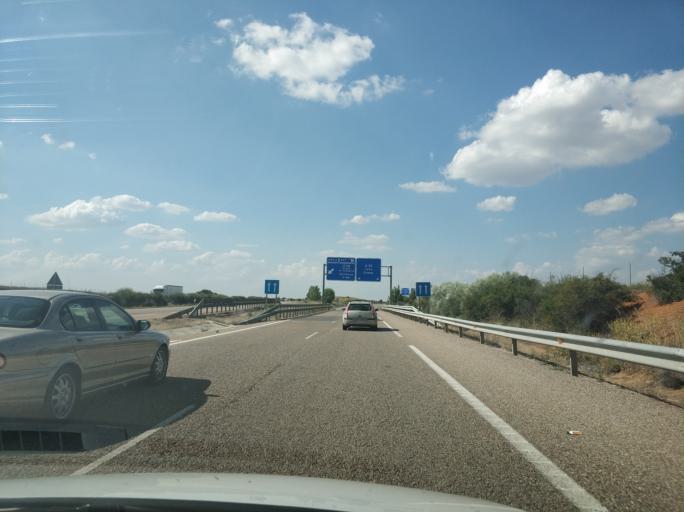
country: ES
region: Castille and Leon
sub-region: Provincia de Zamora
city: San Cristobal de Entrevinas
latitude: 42.0501
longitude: -5.6752
